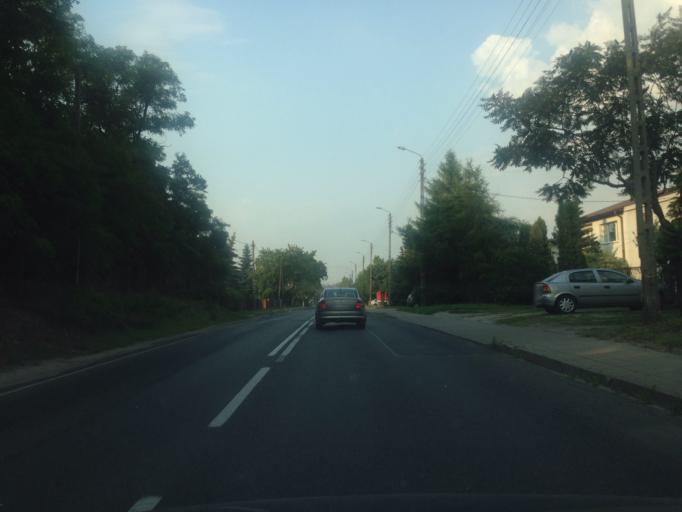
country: PL
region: Kujawsko-Pomorskie
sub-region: Powiat lipnowski
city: Lipno
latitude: 52.8349
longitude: 19.1679
